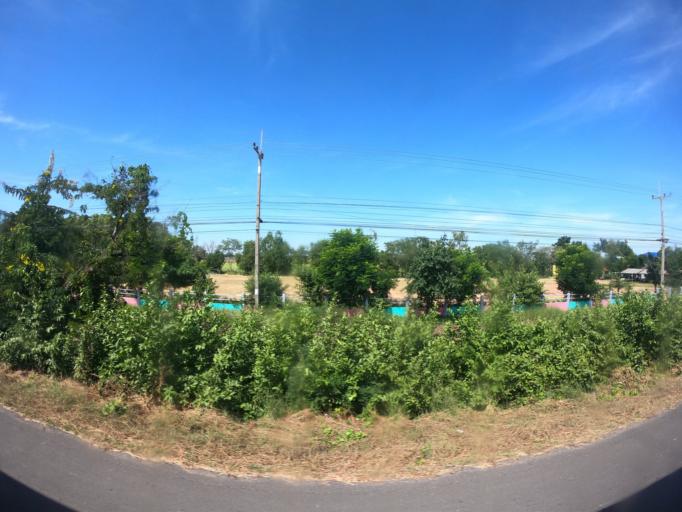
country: TH
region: Nakhon Ratchasima
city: Non Sung
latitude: 15.1947
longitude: 102.3490
